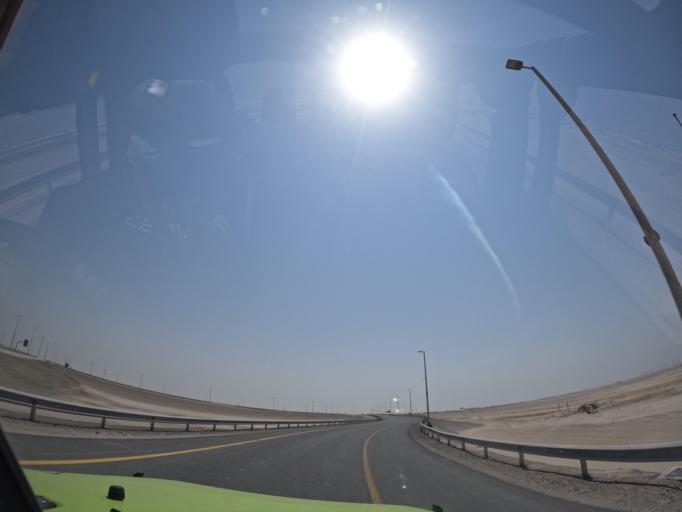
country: AE
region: Abu Dhabi
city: Abu Dhabi
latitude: 24.2496
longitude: 54.4694
